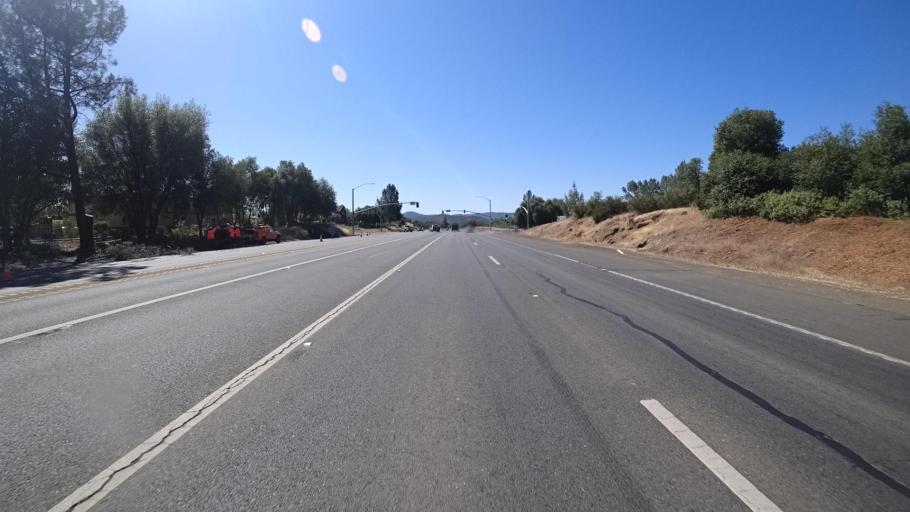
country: US
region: California
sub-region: Lake County
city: Lower Lake
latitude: 38.9311
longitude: -122.6195
